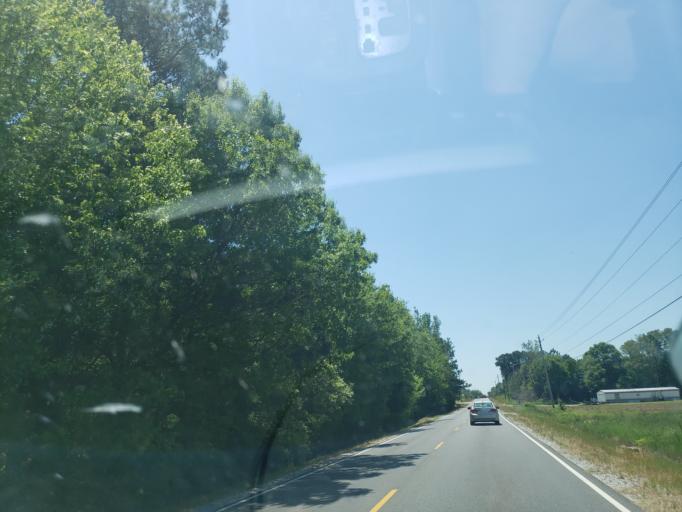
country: US
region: Alabama
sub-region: Madison County
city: Harvest
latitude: 34.8649
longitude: -86.7471
